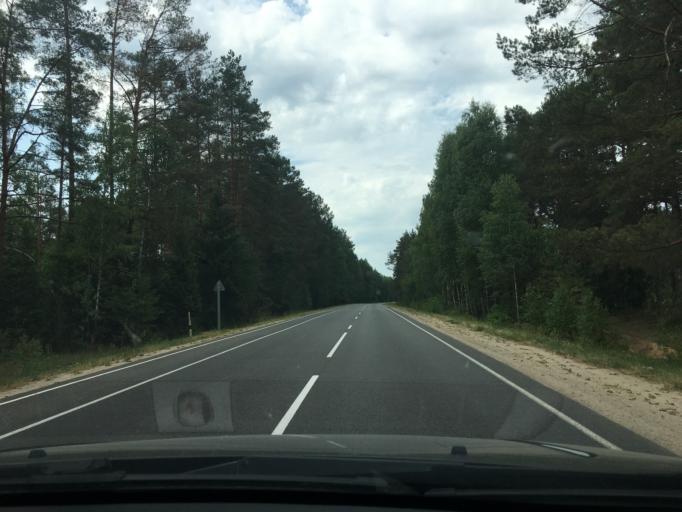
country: LT
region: Alytaus apskritis
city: Druskininkai
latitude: 53.8745
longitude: 24.1222
